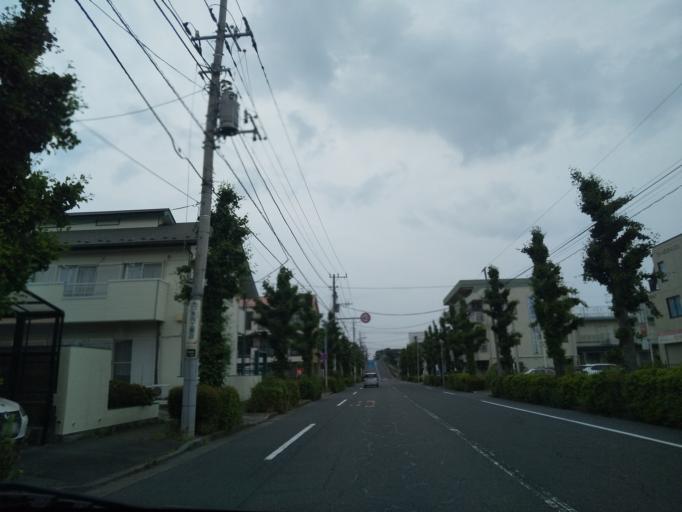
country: JP
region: Tokyo
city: Hino
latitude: 35.6652
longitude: 139.3908
